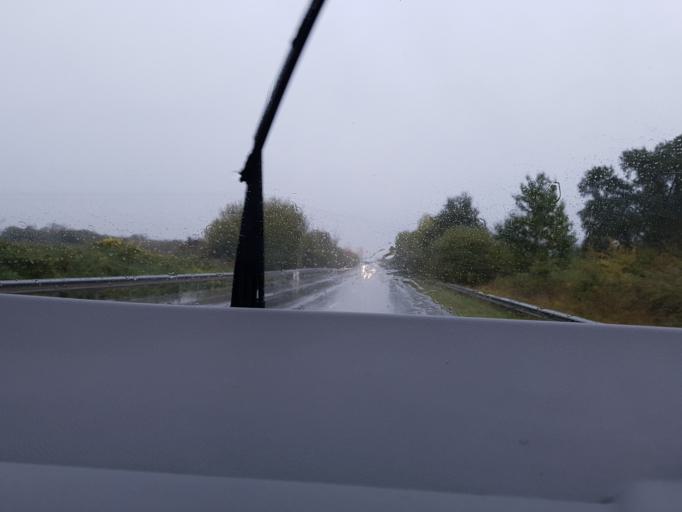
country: FR
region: Aquitaine
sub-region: Departement de la Gironde
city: Saint-Vincent-de-Paul
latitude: 44.9602
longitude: -0.5009
